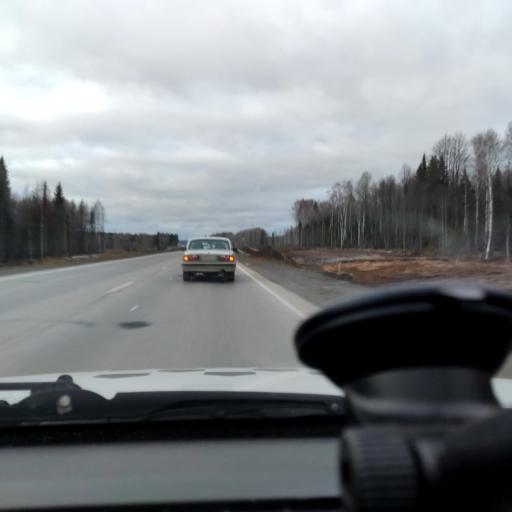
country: RU
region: Perm
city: Polazna
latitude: 58.1320
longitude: 56.4215
